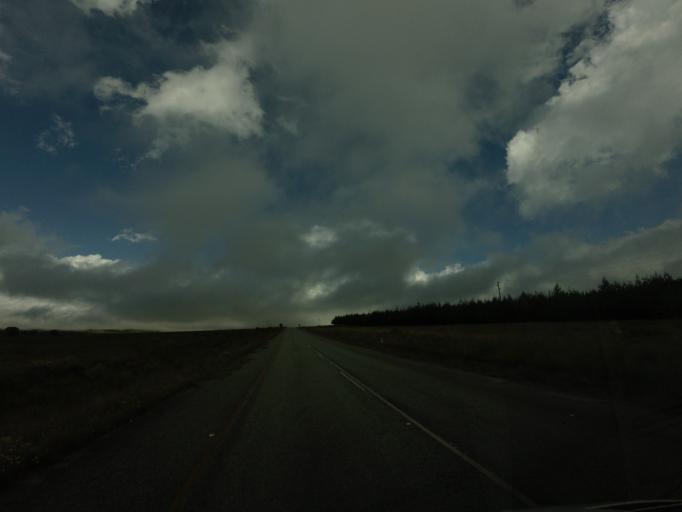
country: ZA
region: Mpumalanga
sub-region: Ehlanzeni District
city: Graksop
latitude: -24.8563
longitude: 30.8734
